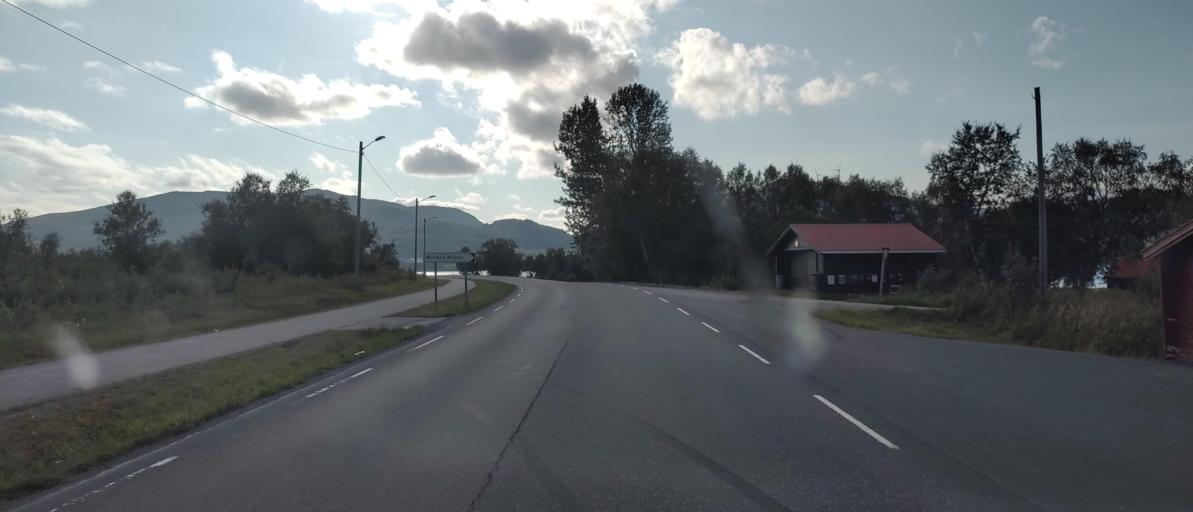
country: NO
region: Nordland
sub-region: Sortland
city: Sortland
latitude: 68.7174
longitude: 15.4465
